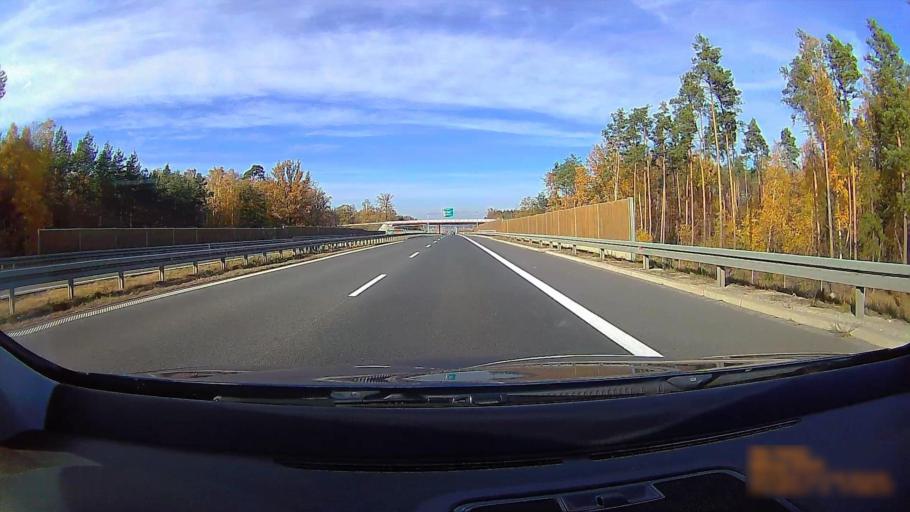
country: PL
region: Greater Poland Voivodeship
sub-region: Powiat ostrowski
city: Ostrow Wielkopolski
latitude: 51.6535
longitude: 17.8677
